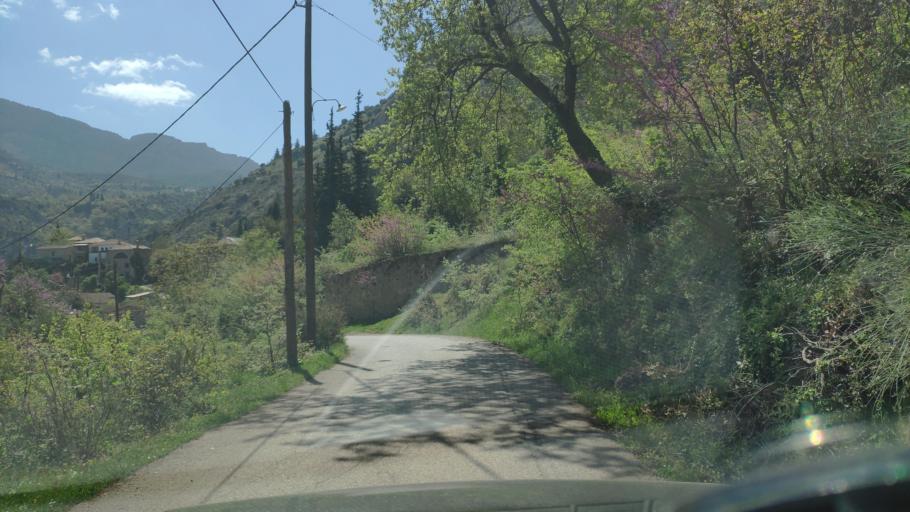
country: GR
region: West Greece
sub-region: Nomos Achaias
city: Aiyira
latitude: 38.0670
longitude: 22.3376
